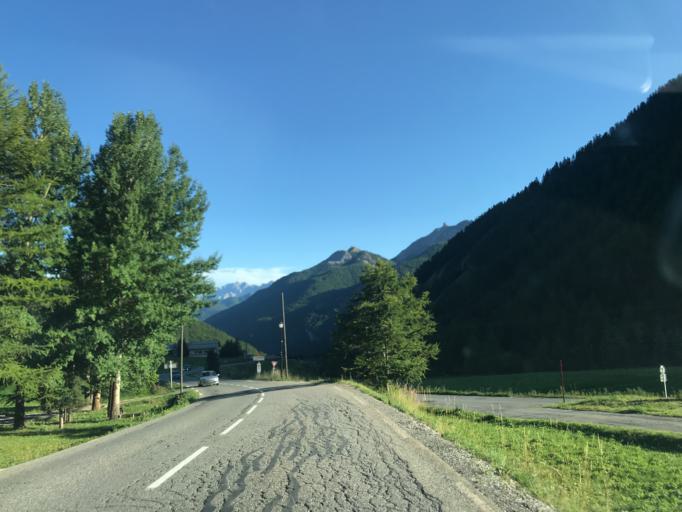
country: FR
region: Provence-Alpes-Cote d'Azur
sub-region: Departement des Hautes-Alpes
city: Villar-Saint-Pancrace
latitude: 44.7909
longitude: 6.7321
